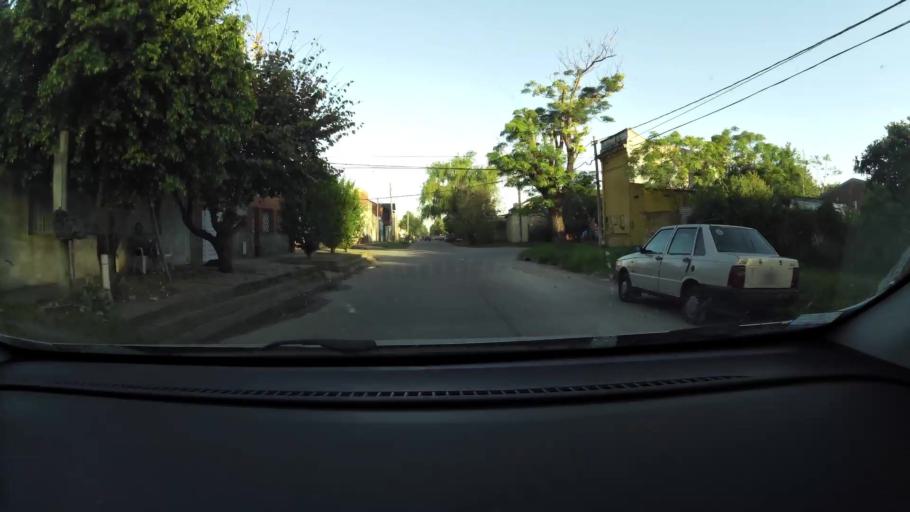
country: AR
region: Santa Fe
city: Santa Fe de la Vera Cruz
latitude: -31.5980
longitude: -60.6888
